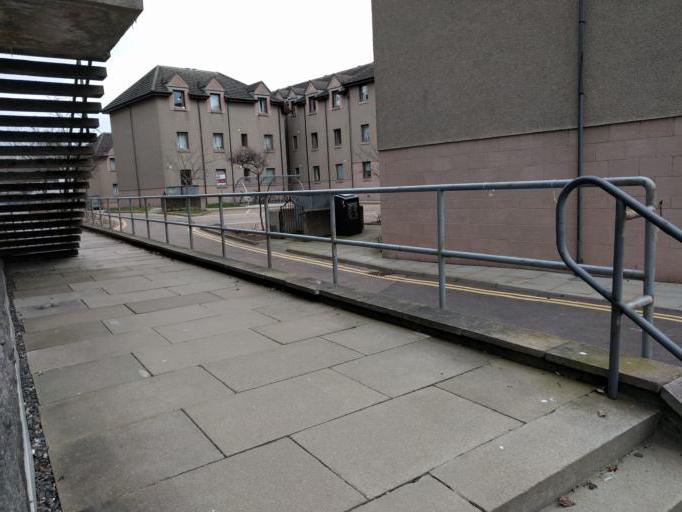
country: GB
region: Scotland
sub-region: Aberdeen City
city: Aberdeen
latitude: 57.1655
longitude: -2.1039
